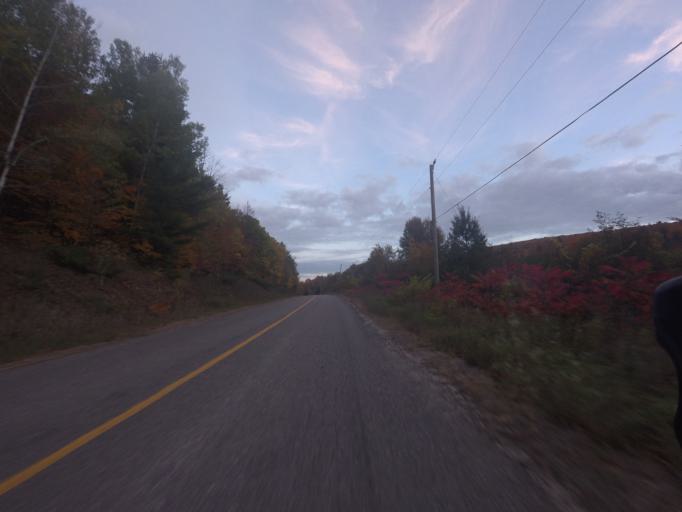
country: CA
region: Ontario
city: Renfrew
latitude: 45.3596
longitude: -76.9654
